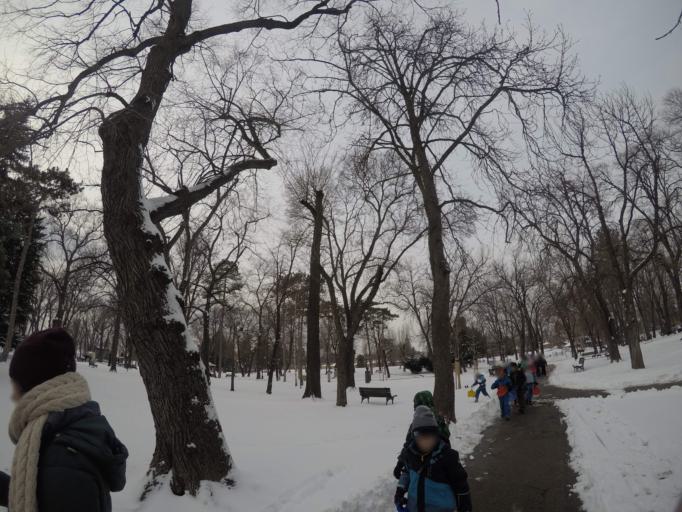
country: RS
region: Central Serbia
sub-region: Belgrade
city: Stari Grad
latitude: 44.8207
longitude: 20.4531
